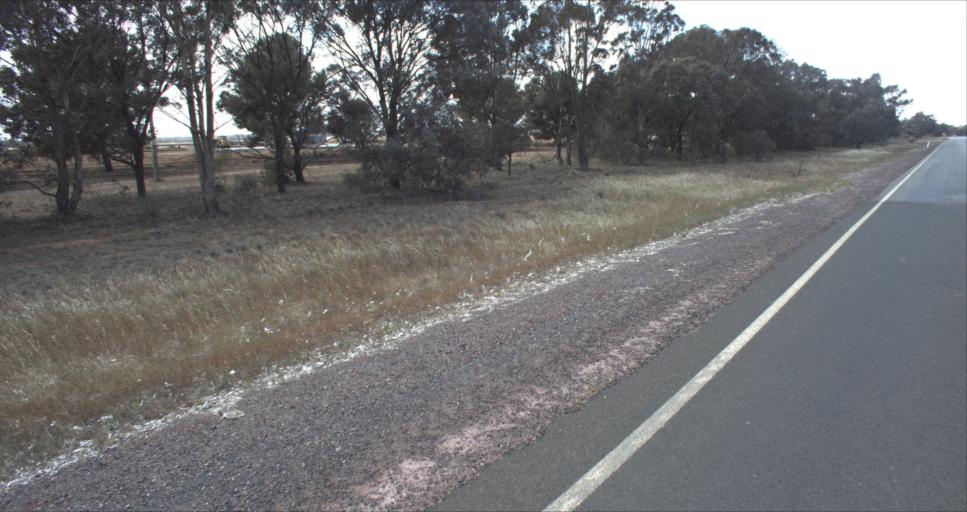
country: AU
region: New South Wales
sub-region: Murrumbidgee Shire
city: Darlington Point
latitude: -34.5900
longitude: 146.1637
